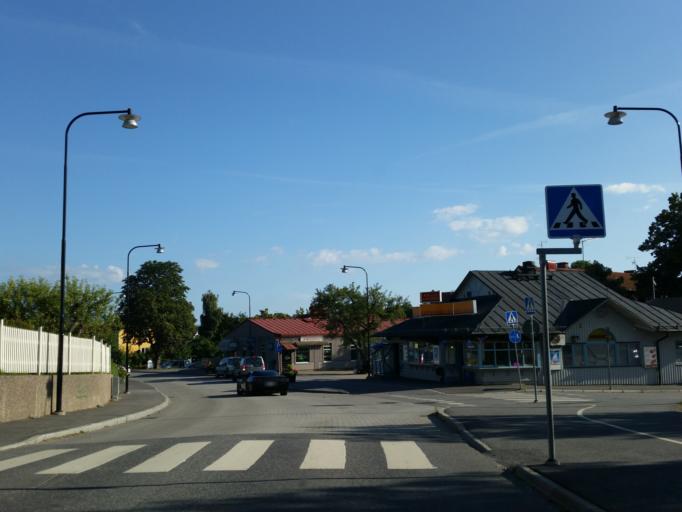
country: SE
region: Soedermanland
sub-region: Trosa Kommun
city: Trosa
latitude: 58.8970
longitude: 17.5498
